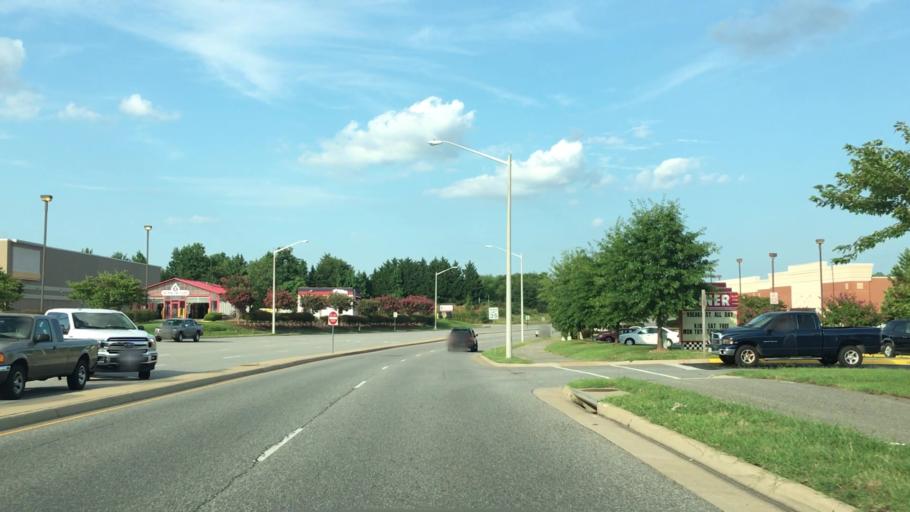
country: US
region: Virginia
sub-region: Stafford County
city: Falmouth
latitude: 38.3054
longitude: -77.5089
